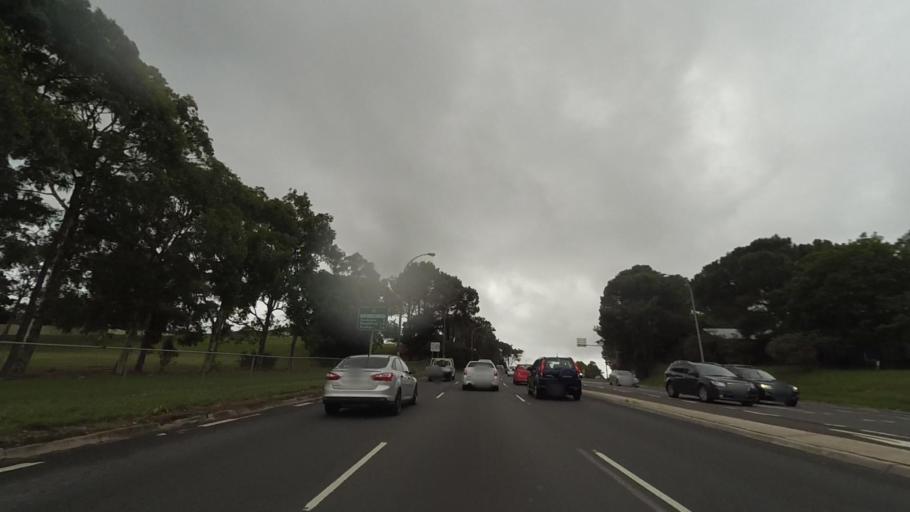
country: AU
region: New South Wales
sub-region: Sutherland Shire
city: Caringbah
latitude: -34.0185
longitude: 151.1219
